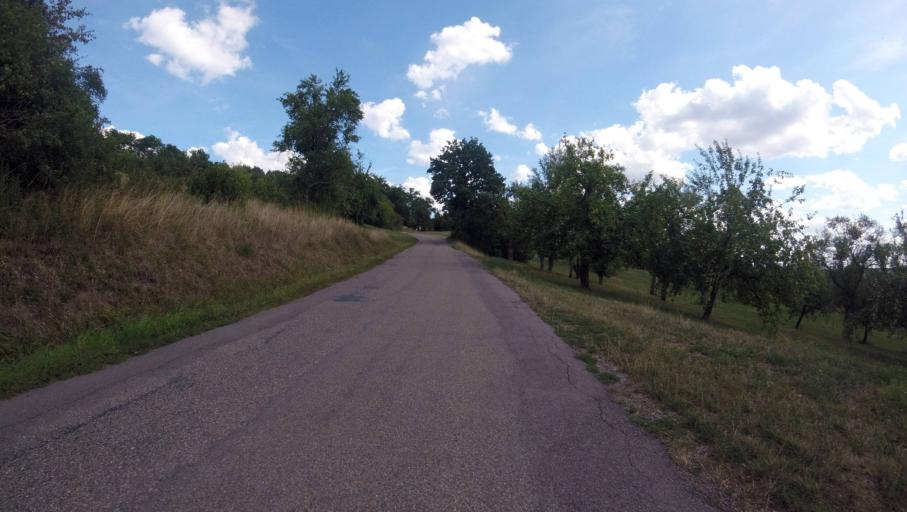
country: DE
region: Baden-Wuerttemberg
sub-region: Regierungsbezirk Stuttgart
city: Aspach
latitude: 48.9841
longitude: 9.4120
